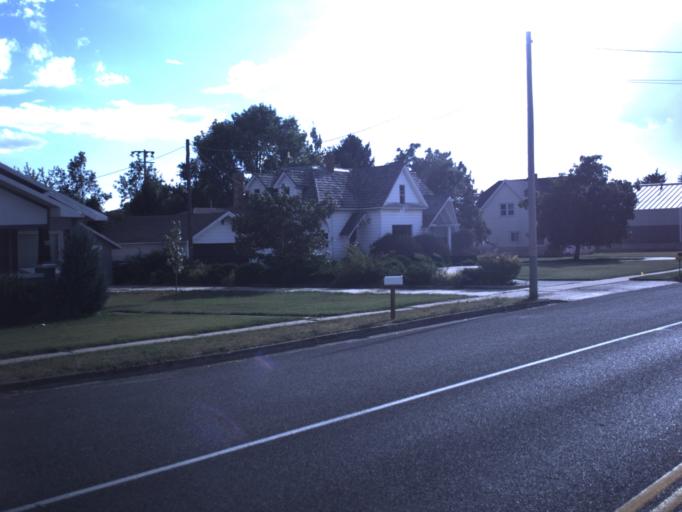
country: US
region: Utah
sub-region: Cache County
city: Lewiston
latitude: 41.9759
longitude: -111.8539
